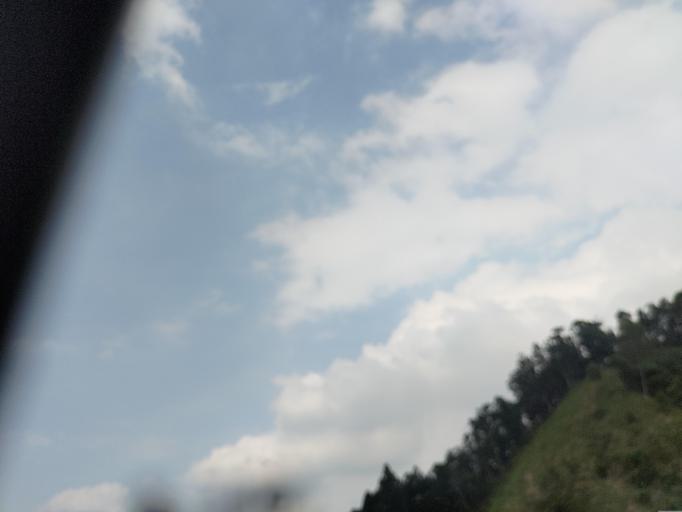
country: TW
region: Taiwan
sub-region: Hsinchu
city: Hsinchu
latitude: 24.6204
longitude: 121.0493
